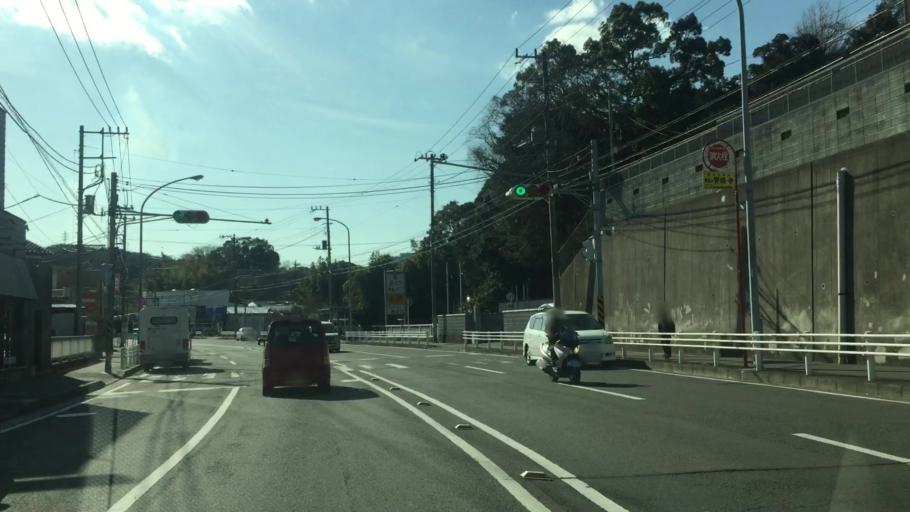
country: JP
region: Kanagawa
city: Zushi
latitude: 35.3633
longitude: 139.6080
